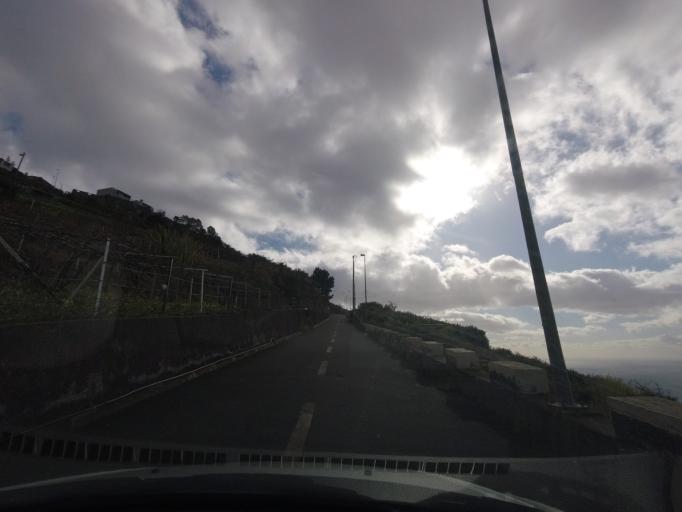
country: PT
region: Madeira
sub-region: Ribeira Brava
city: Campanario
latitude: 32.6618
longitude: -17.0221
